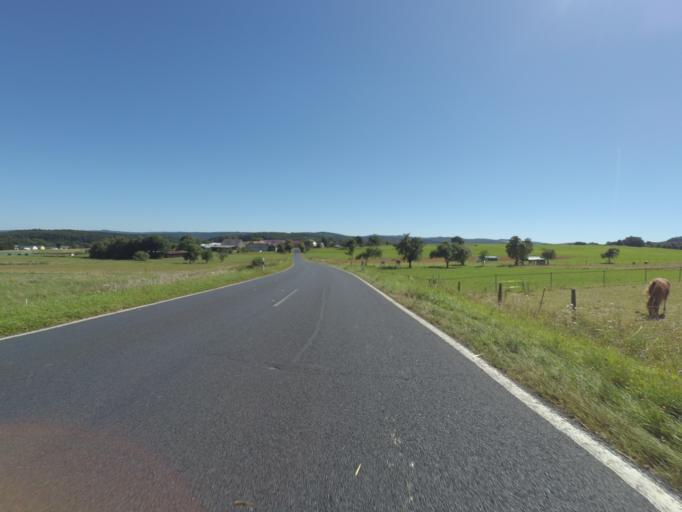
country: DE
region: Rheinland-Pfalz
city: Uxheim
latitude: 50.3271
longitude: 6.7239
